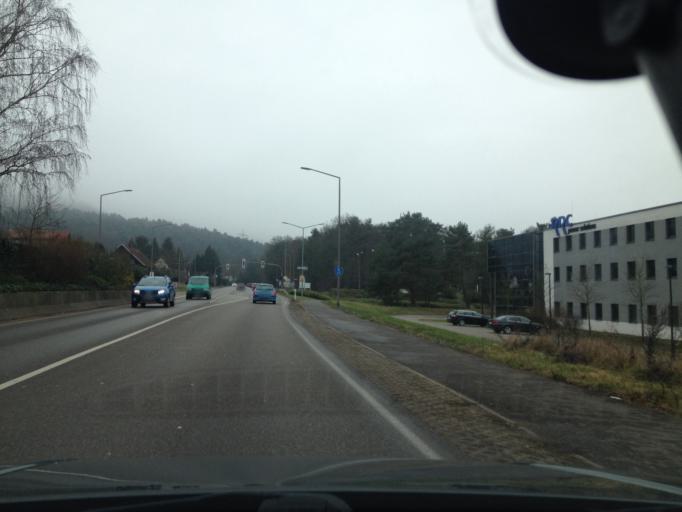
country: DE
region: Saarland
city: Homburg
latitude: 49.3070
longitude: 7.3317
